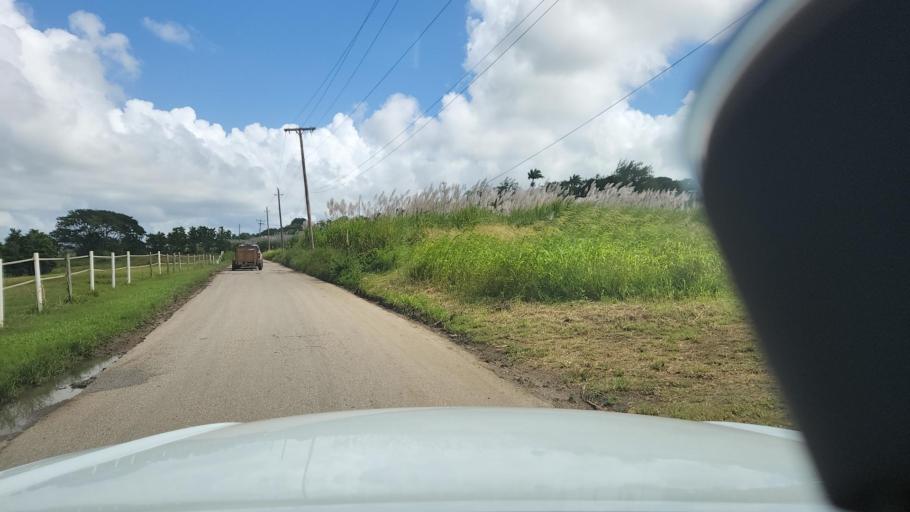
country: BB
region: Saint Thomas
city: Welchman Hall
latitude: 13.1599
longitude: -59.5559
